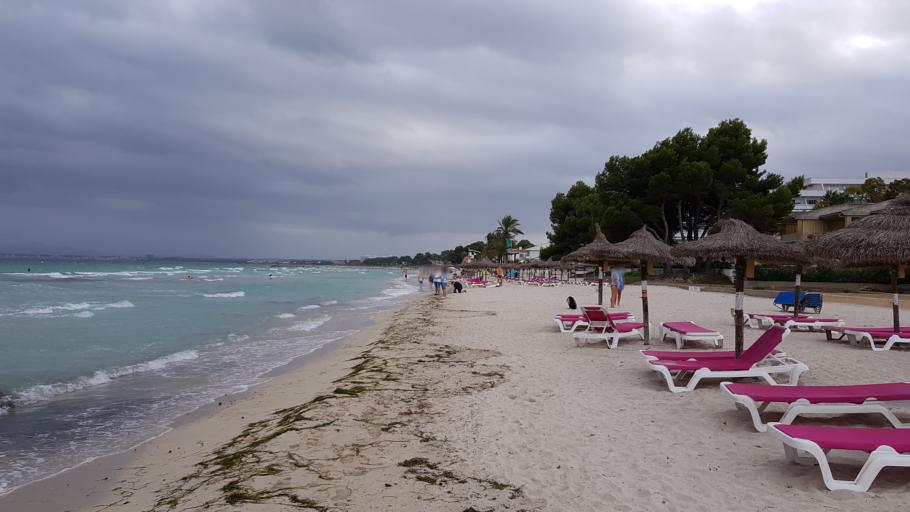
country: ES
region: Balearic Islands
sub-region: Illes Balears
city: Port d'Alcudia
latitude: 39.8190
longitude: 3.1168
